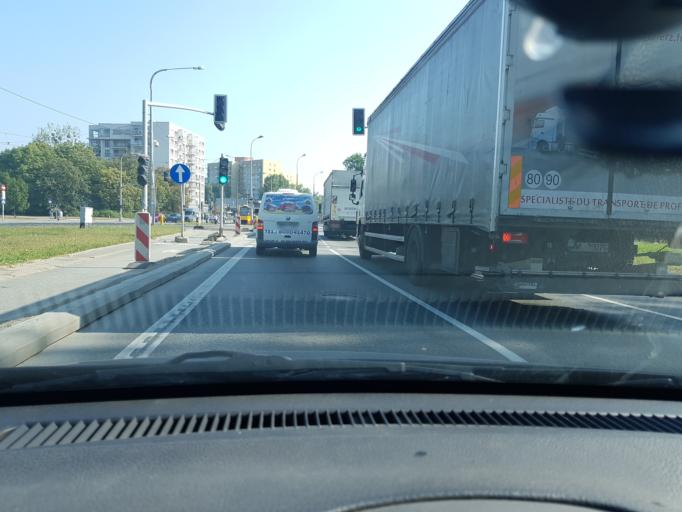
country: PL
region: Masovian Voivodeship
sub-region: Warszawa
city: Ochota
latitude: 52.2289
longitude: 20.9500
